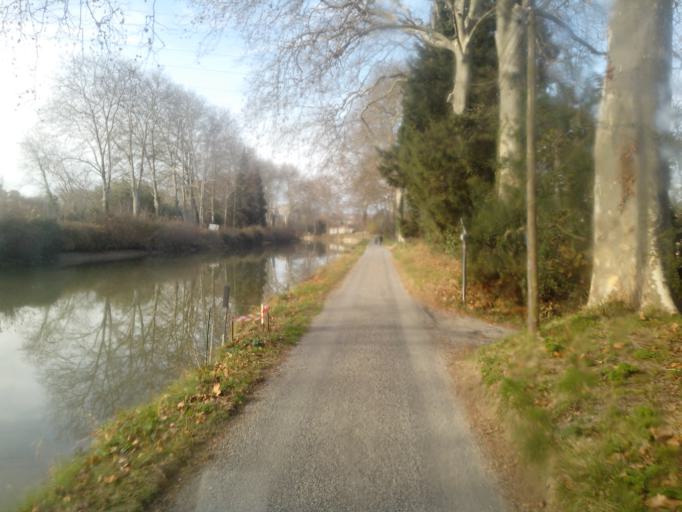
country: FR
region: Languedoc-Roussillon
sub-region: Departement de l'Aude
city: Castelnaudary
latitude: 43.3090
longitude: 1.9685
